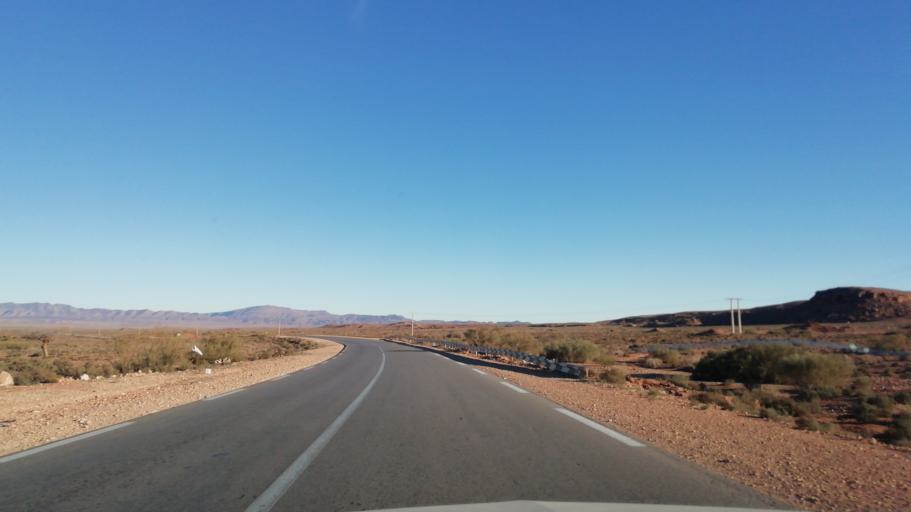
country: DZ
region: El Bayadh
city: El Abiodh Sidi Cheikh
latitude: 33.1675
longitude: 0.4623
